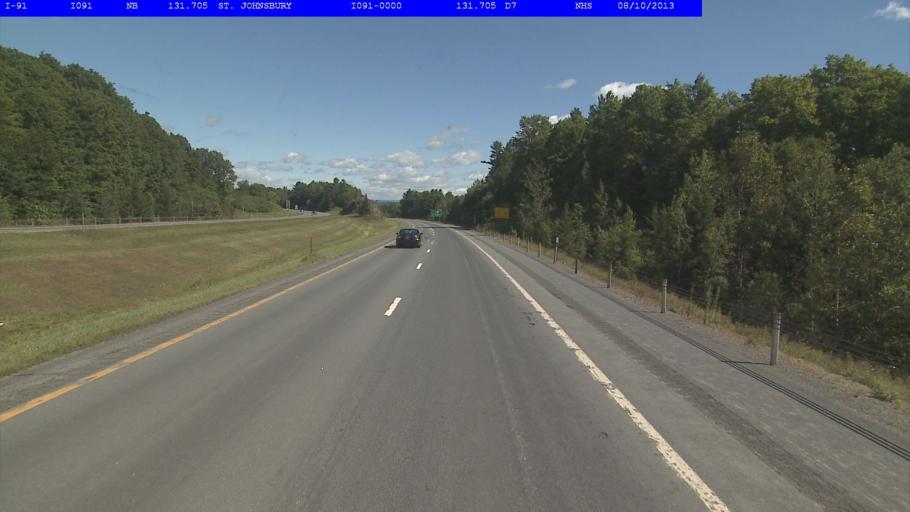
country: US
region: Vermont
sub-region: Caledonia County
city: St Johnsbury
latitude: 44.4415
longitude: -72.0250
